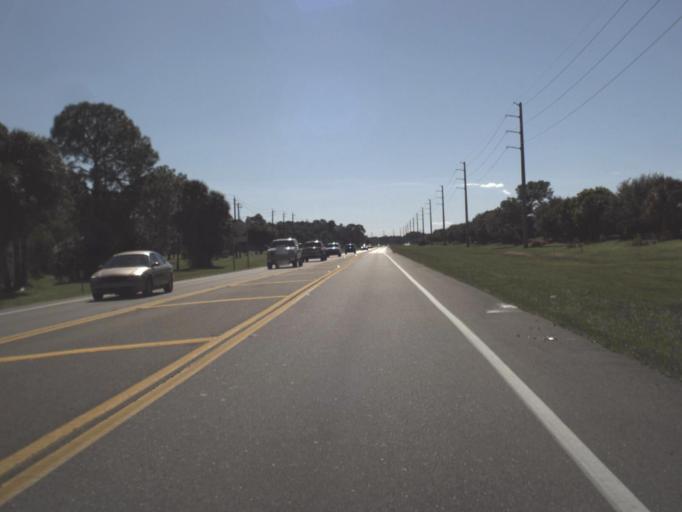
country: US
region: Florida
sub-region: Lee County
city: Gateway
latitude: 26.6033
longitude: -81.7502
